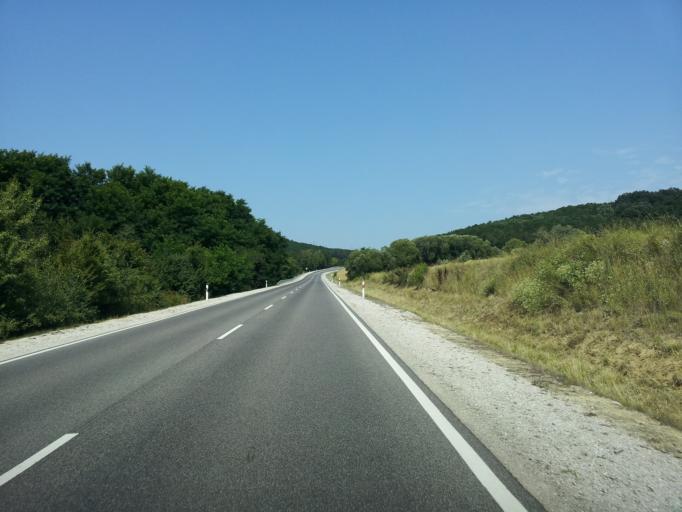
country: HU
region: Zala
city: Pacsa
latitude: 46.8096
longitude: 17.0664
